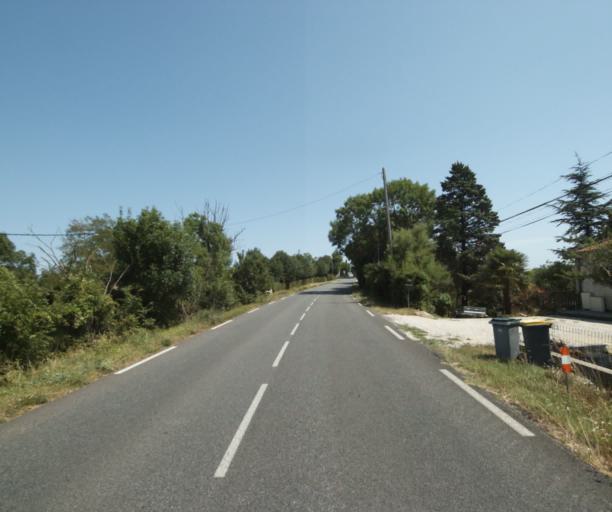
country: FR
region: Midi-Pyrenees
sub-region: Departement de la Haute-Garonne
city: Saint-Felix-Lauragais
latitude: 43.4523
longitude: 1.8788
